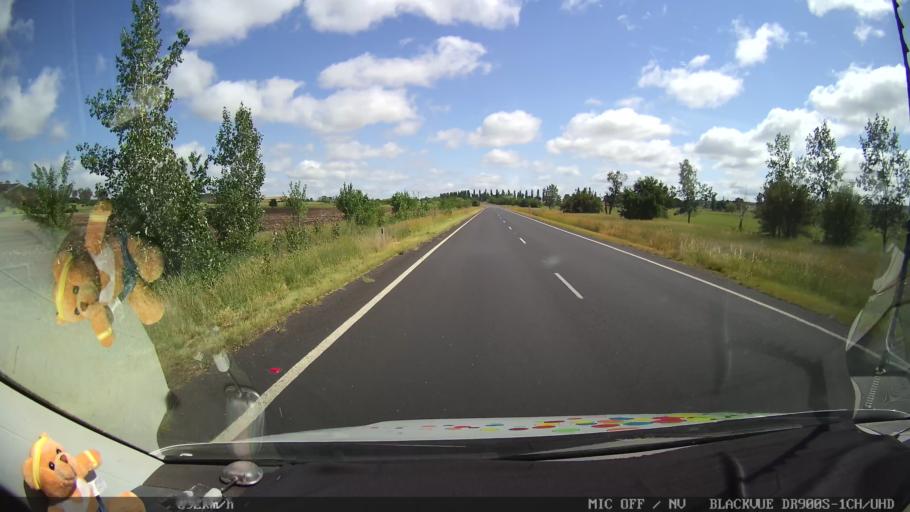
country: AU
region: New South Wales
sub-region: Glen Innes Severn
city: Glen Innes
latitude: -29.8521
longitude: 151.7372
